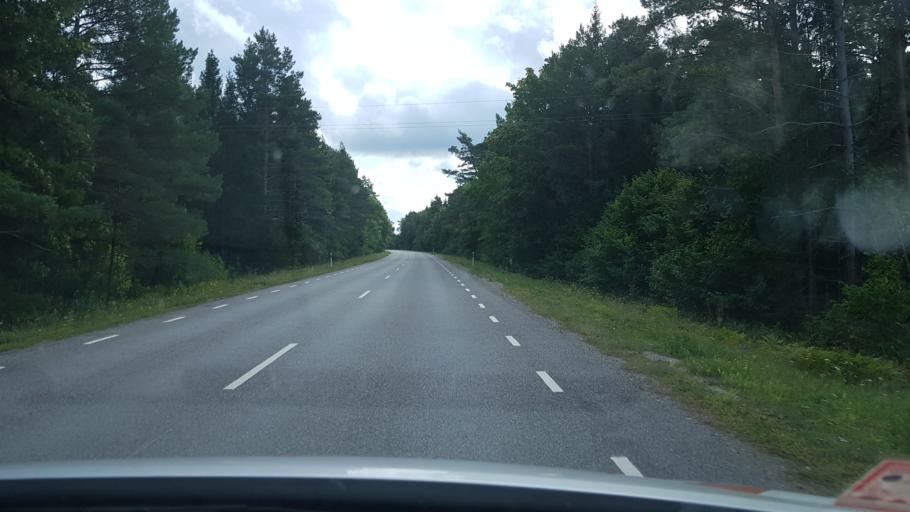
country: EE
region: Saare
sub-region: Kuressaare linn
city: Kuressaare
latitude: 58.3560
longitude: 22.0682
